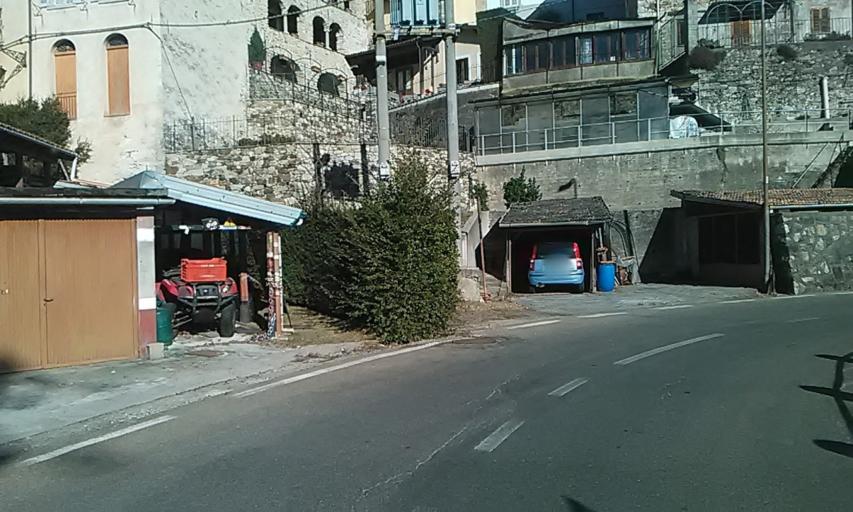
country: IT
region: Piedmont
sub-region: Provincia di Vercelli
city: Civiasco
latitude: 45.8076
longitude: 8.2944
